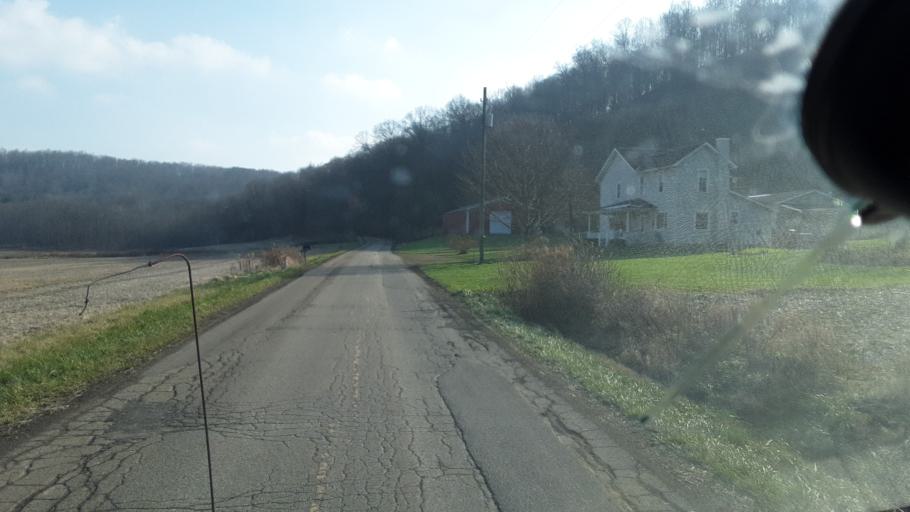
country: US
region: Ohio
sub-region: Knox County
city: Oak Hill
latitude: 40.4278
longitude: -82.2006
